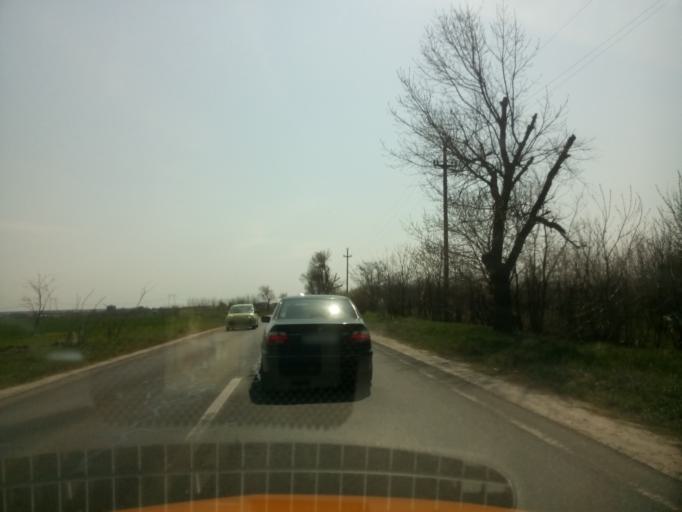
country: RO
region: Ilfov
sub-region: Comuna Glina
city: Glina
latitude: 44.3299
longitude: 26.2530
